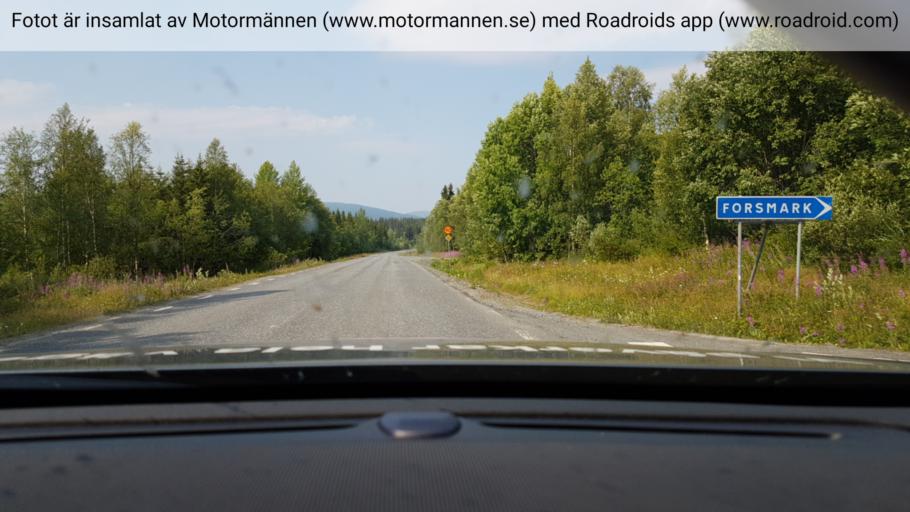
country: SE
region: Vaesterbotten
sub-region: Vilhelmina Kommun
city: Sjoberg
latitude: 65.4810
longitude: 15.8771
